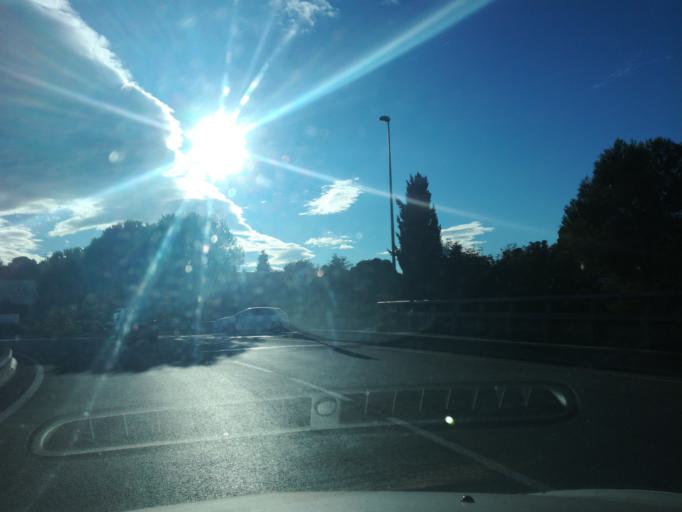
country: FR
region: Provence-Alpes-Cote d'Azur
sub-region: Departement des Alpes-Maritimes
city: Mouans-Sartoux
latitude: 43.6122
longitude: 6.9674
